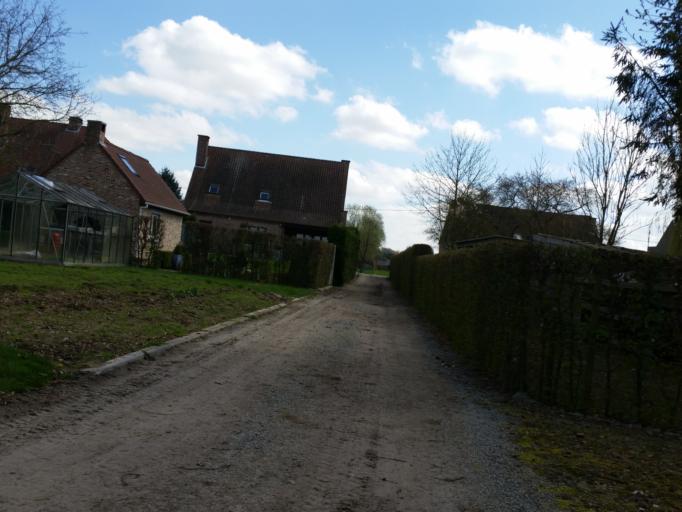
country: BE
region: Flanders
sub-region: Provincie Vlaams-Brabant
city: Boortmeerbeek
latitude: 50.9544
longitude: 4.5739
